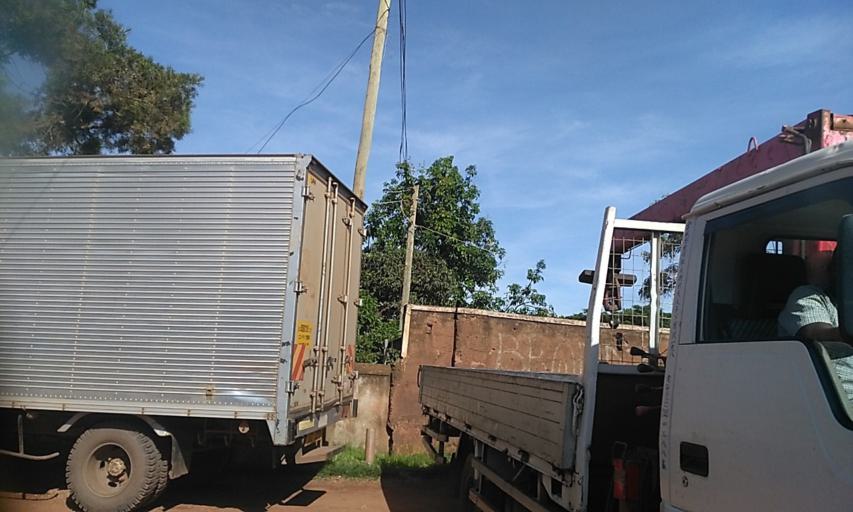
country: UG
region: Central Region
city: Kampala Central Division
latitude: 0.3219
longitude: 32.5662
